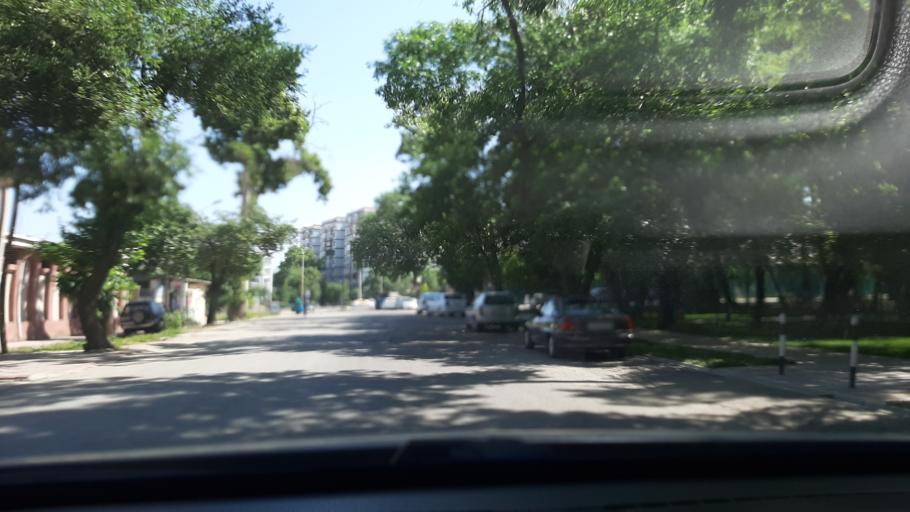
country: TJ
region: Dushanbe
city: Dushanbe
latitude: 38.5572
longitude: 68.7573
